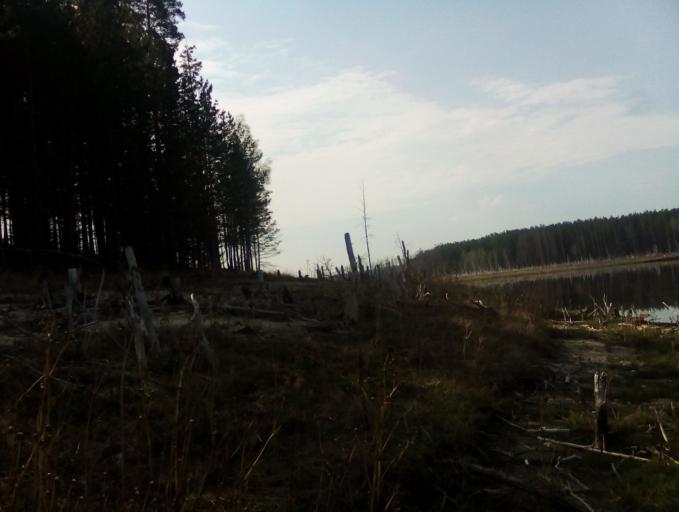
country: RU
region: Chelyabinsk
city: Nizhniy Ufaley
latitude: 55.7544
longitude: 60.1264
